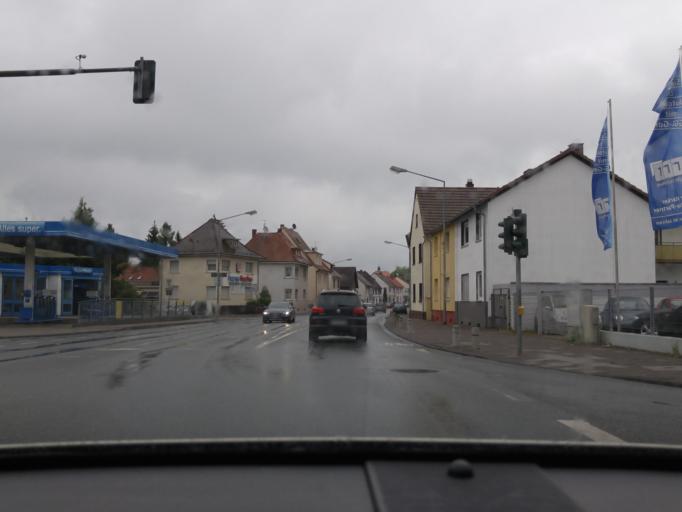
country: DE
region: Hesse
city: Dreieich
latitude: 50.0130
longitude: 8.6923
